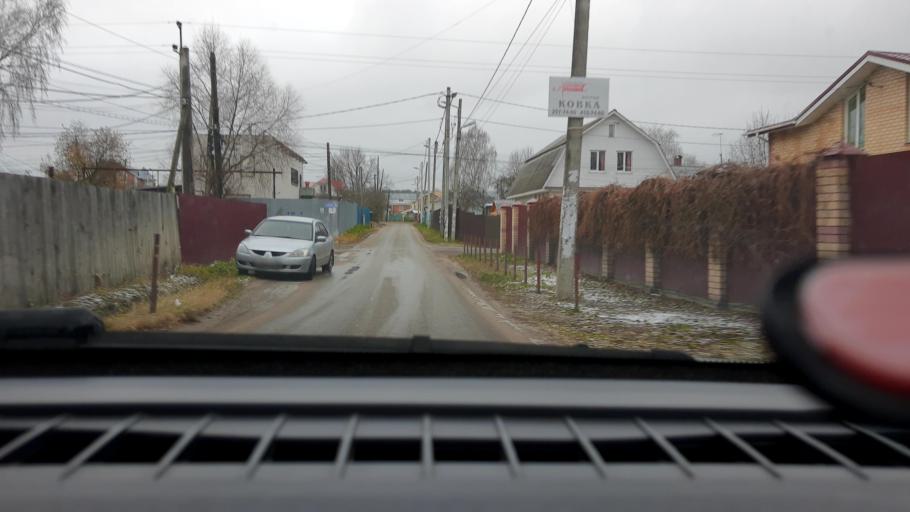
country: RU
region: Nizjnij Novgorod
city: Burevestnik
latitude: 56.2048
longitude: 43.7982
